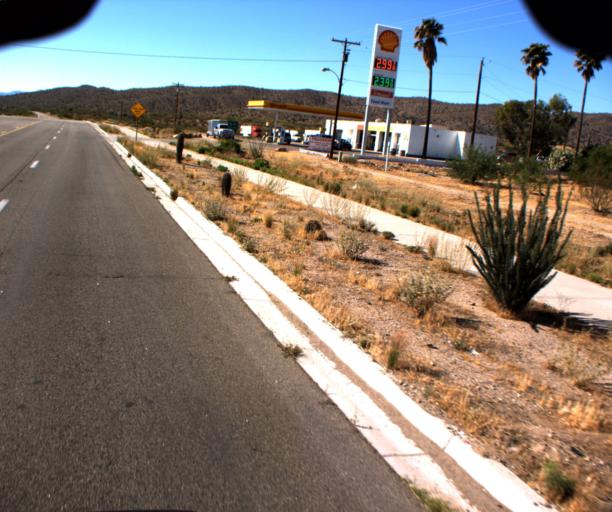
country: US
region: Arizona
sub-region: Yavapai County
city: Bagdad
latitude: 34.7005
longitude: -113.6100
